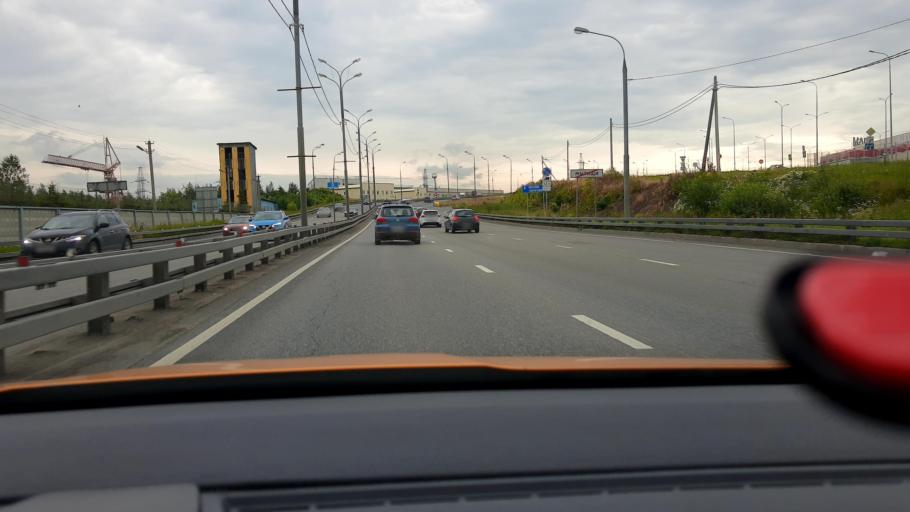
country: RU
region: Moscow
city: Vatutino
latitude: 55.9144
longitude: 37.6785
